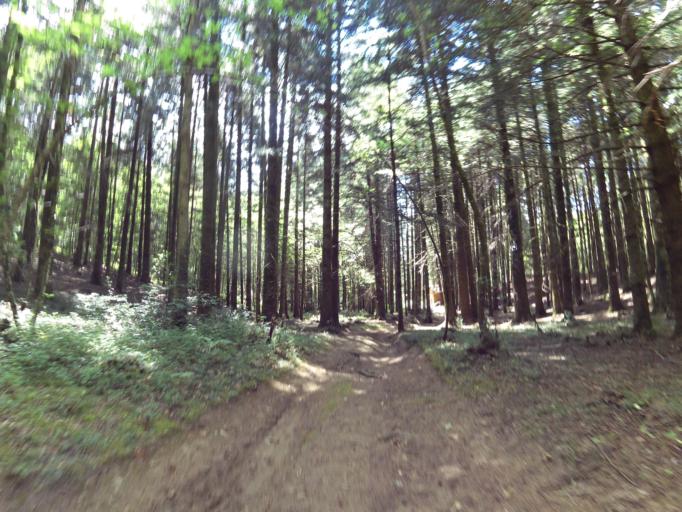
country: IT
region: Calabria
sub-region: Provincia di Vibo-Valentia
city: Mongiana
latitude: 38.5379
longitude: 16.3303
